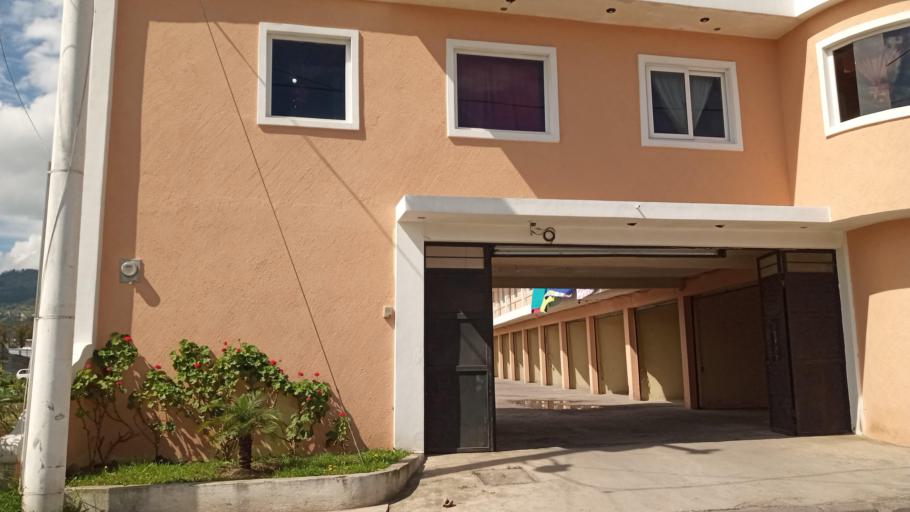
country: GT
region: Quetzaltenango
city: Quetzaltenango
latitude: 14.8444
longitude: -91.5090
